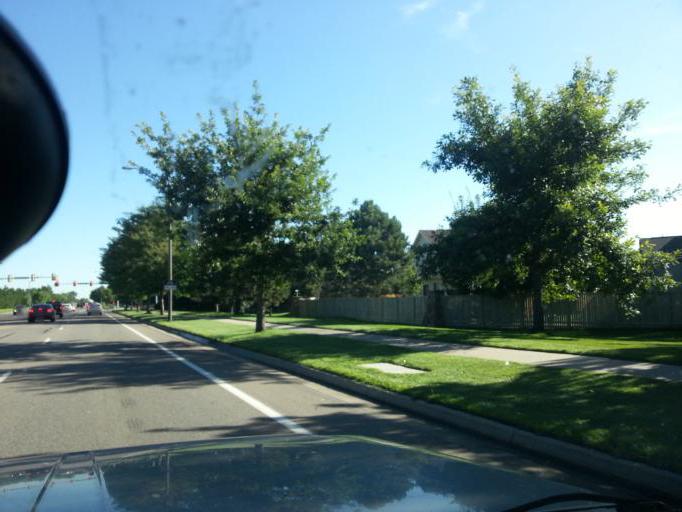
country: US
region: Colorado
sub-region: Larimer County
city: Fort Collins
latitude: 40.5137
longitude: -105.0393
